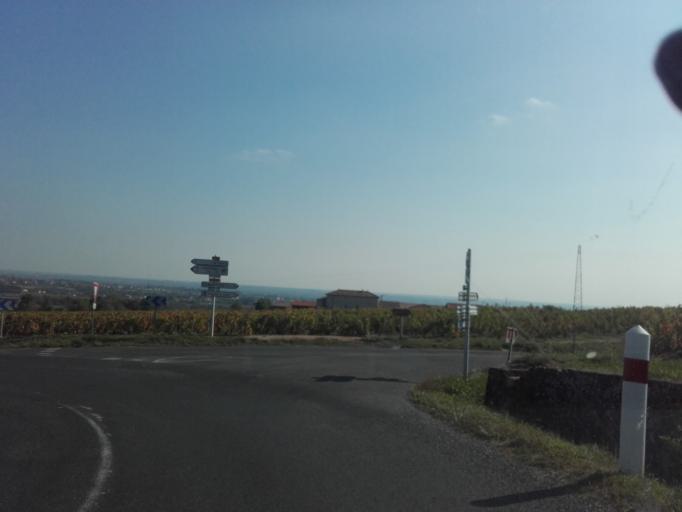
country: FR
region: Rhone-Alpes
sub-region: Departement du Rhone
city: Fleurie
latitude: 46.2086
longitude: 4.7199
